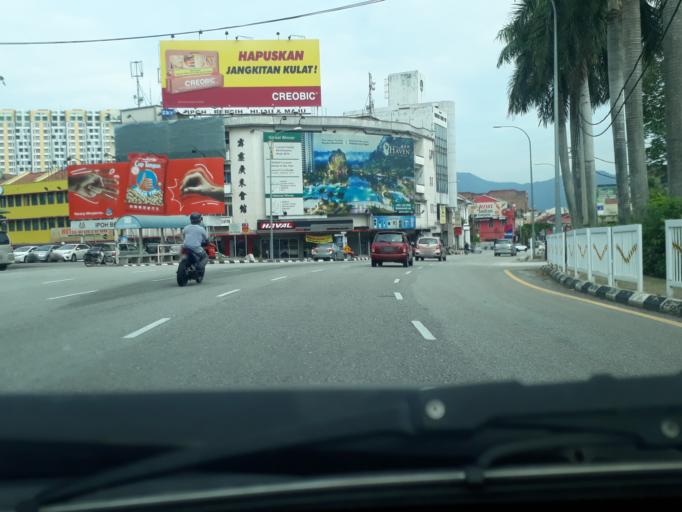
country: MY
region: Perak
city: Ipoh
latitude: 4.5920
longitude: 101.0869
